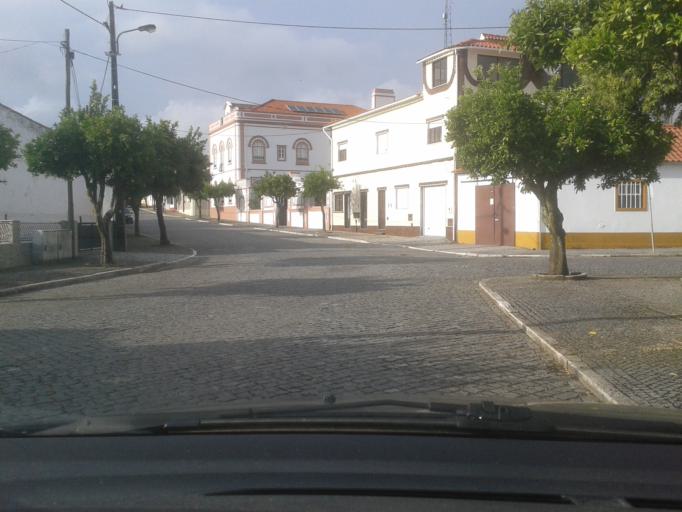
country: PT
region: Portalegre
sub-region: Avis
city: Avis
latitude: 39.0522
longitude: -7.8914
